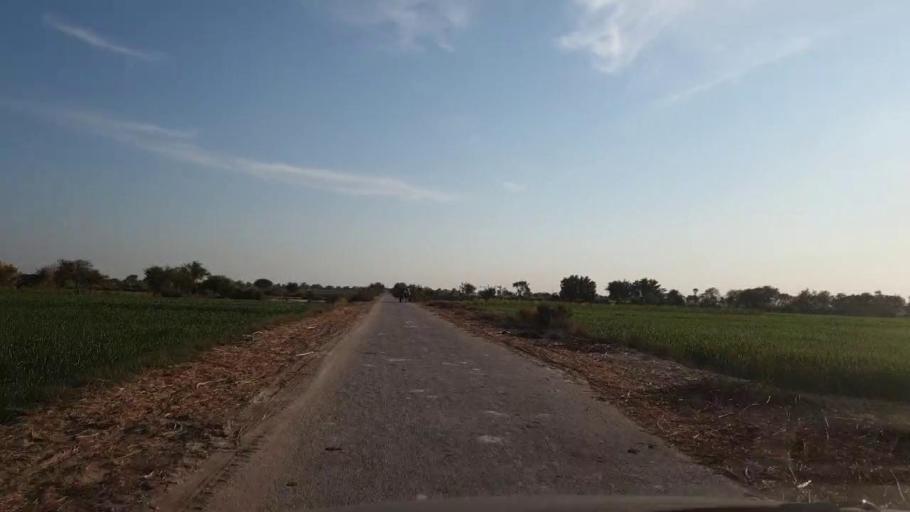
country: PK
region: Sindh
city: Khadro
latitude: 26.2007
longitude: 68.7467
